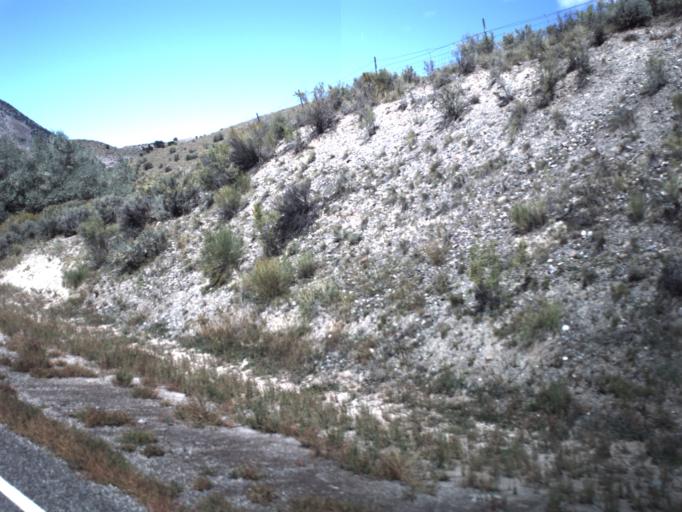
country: US
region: Utah
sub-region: Piute County
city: Junction
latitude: 38.1691
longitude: -112.0561
